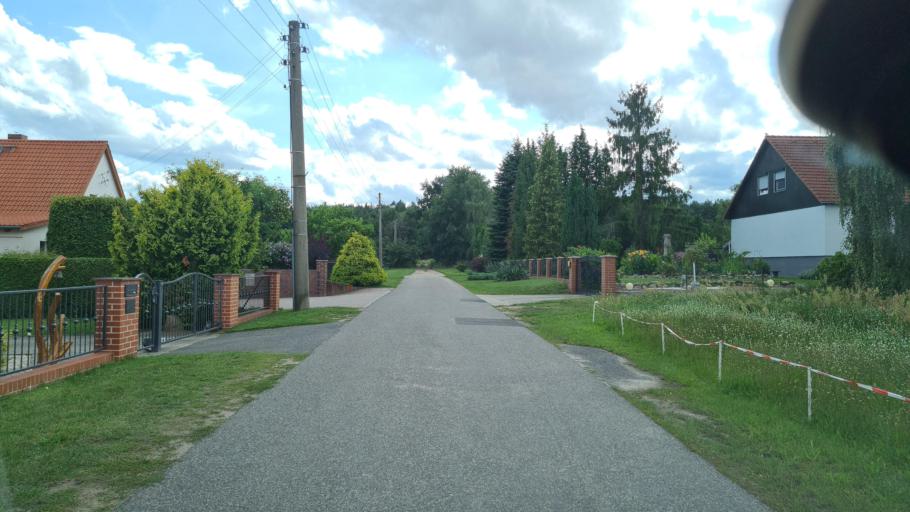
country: DE
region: Brandenburg
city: Drebkau
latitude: 51.6335
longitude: 14.2827
